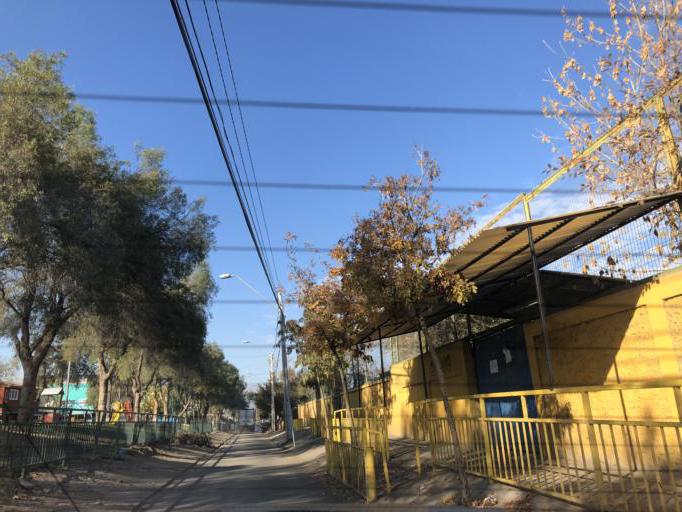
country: CL
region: Santiago Metropolitan
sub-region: Provincia de Cordillera
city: Puente Alto
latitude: -33.6171
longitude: -70.5881
